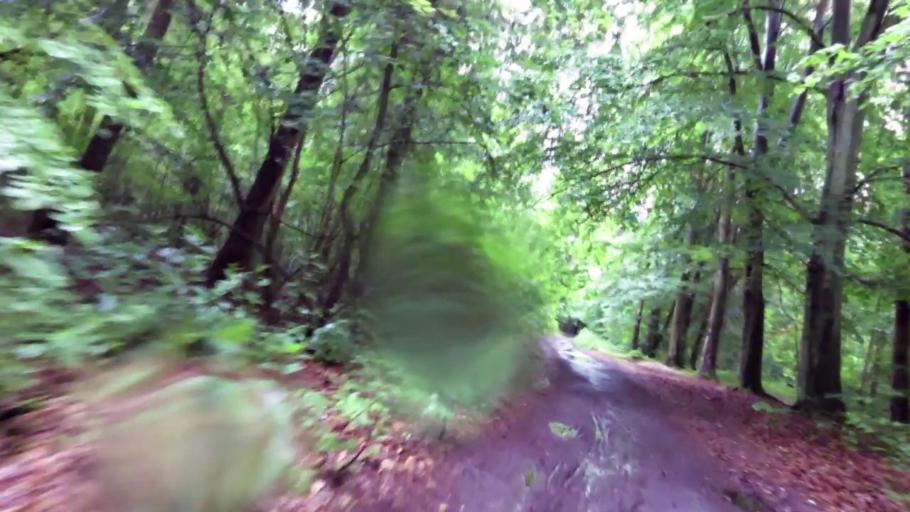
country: PL
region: West Pomeranian Voivodeship
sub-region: Powiat koszalinski
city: Mielno
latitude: 54.2562
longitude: 16.0348
